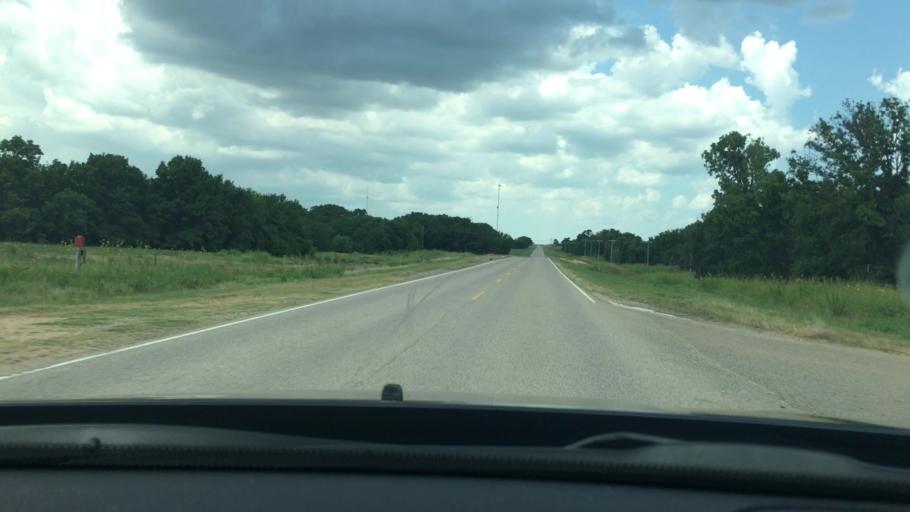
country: US
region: Oklahoma
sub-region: Johnston County
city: Tishomingo
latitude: 34.4193
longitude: -96.6359
